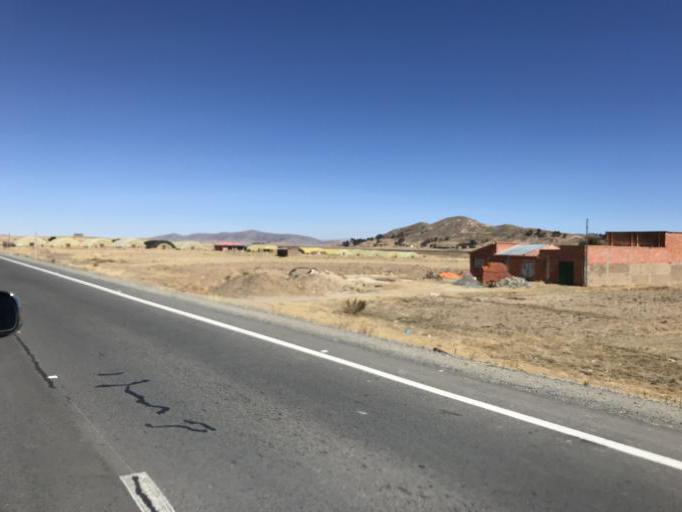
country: BO
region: La Paz
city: Huarina
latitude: -16.2165
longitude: -68.5888
